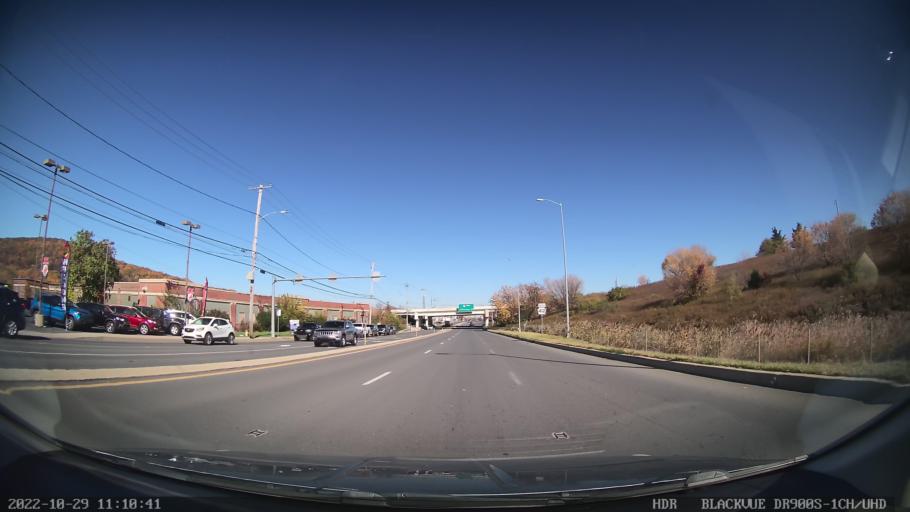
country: US
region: Pennsylvania
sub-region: Northampton County
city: Hellertown
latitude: 40.5949
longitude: -75.3402
